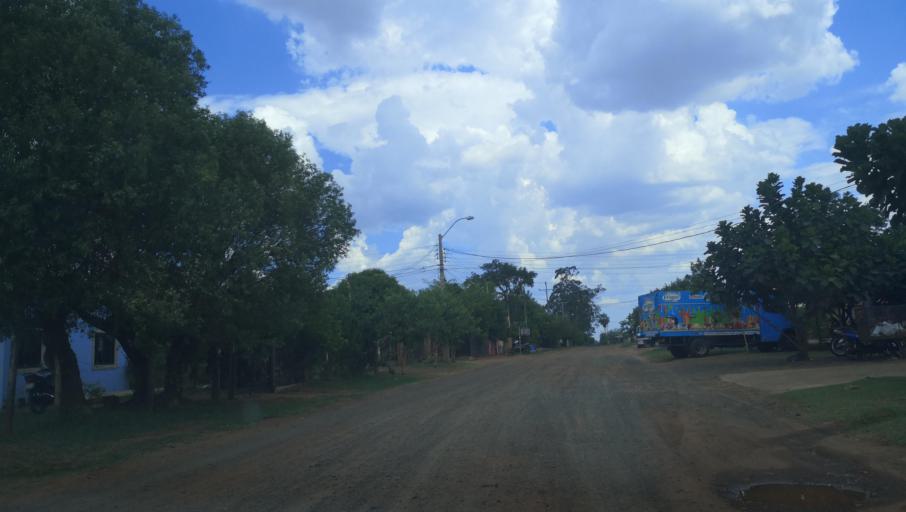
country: PY
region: Misiones
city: Santa Maria
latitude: -26.8972
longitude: -57.0389
